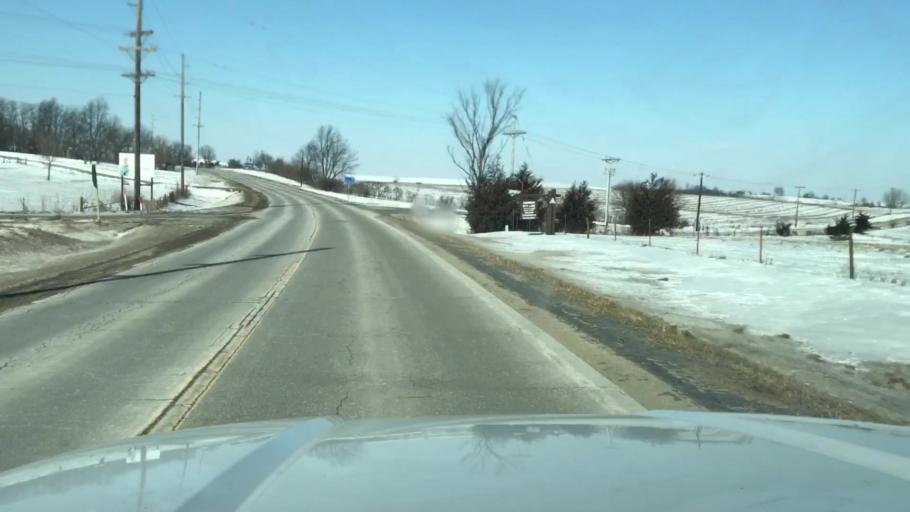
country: US
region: Missouri
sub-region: Andrew County
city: Savannah
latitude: 39.9580
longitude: -94.8510
